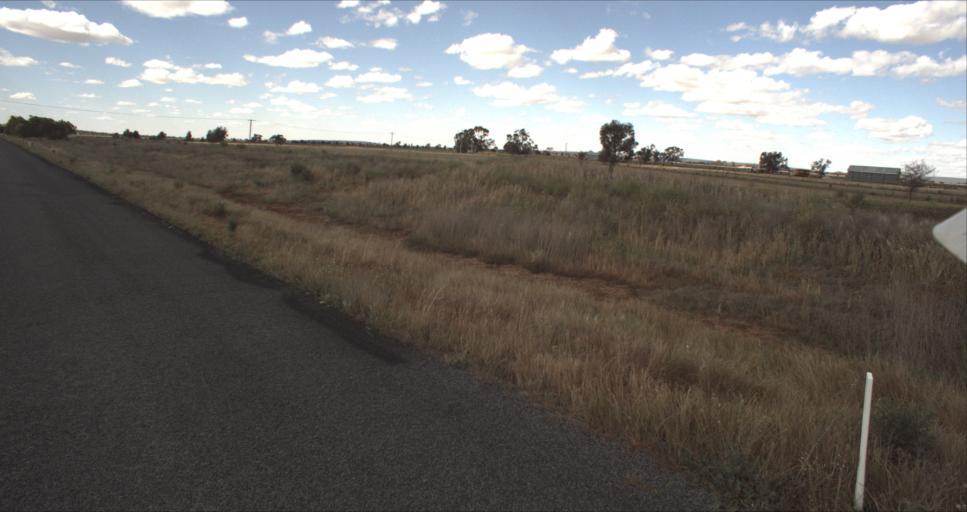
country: AU
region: New South Wales
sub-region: Leeton
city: Leeton
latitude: -34.4480
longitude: 146.2551
